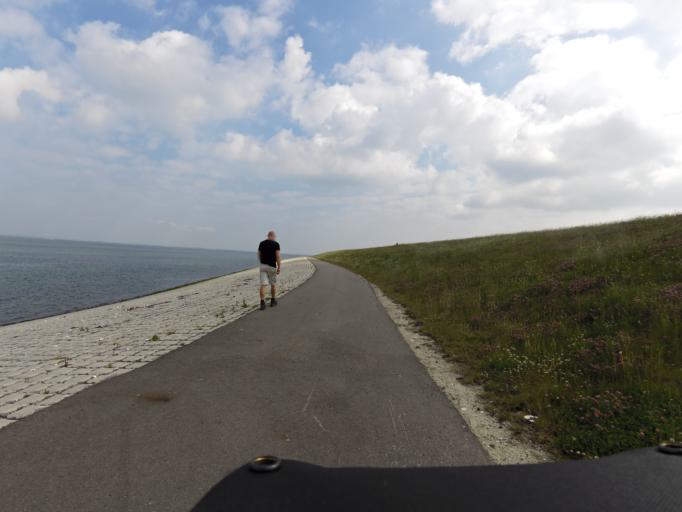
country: NL
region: Zeeland
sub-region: Gemeente Noord-Beveland
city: Kamperland
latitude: 51.5990
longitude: 3.7777
